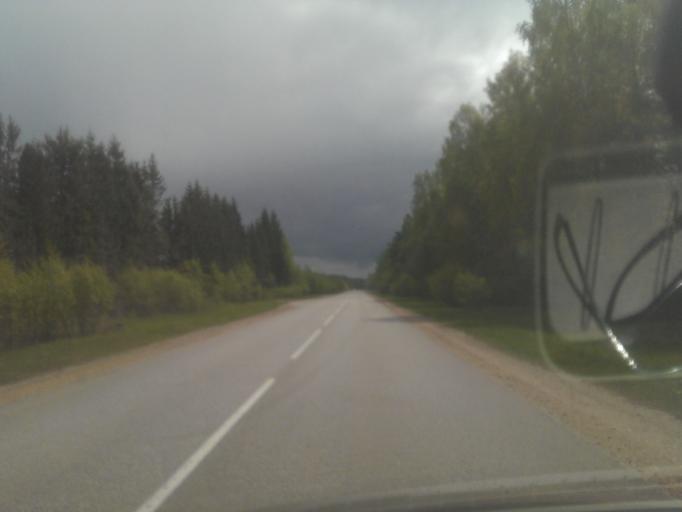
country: LV
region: Ventspils Rajons
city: Piltene
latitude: 57.1726
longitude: 21.6676
